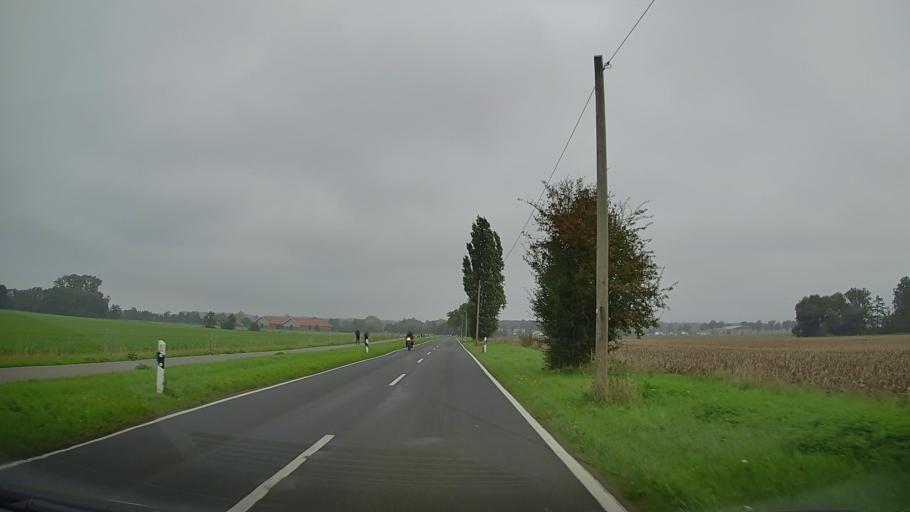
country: DE
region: Mecklenburg-Vorpommern
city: Neubukow
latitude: 54.0683
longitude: 11.6293
